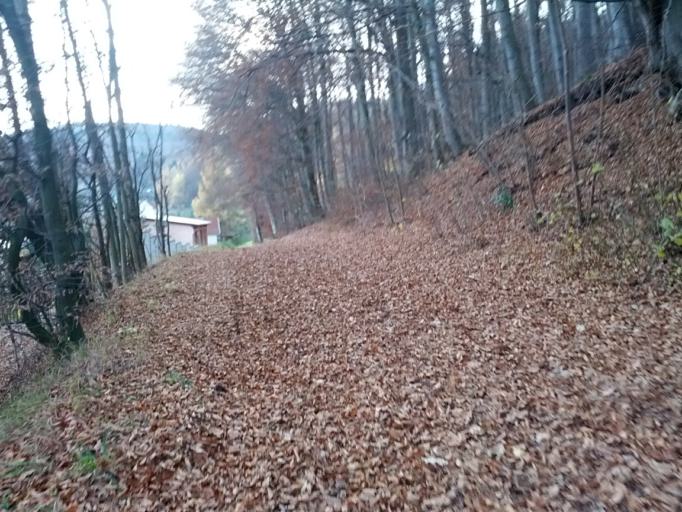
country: DE
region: Thuringia
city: Ruhla
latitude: 50.9284
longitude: 10.3506
